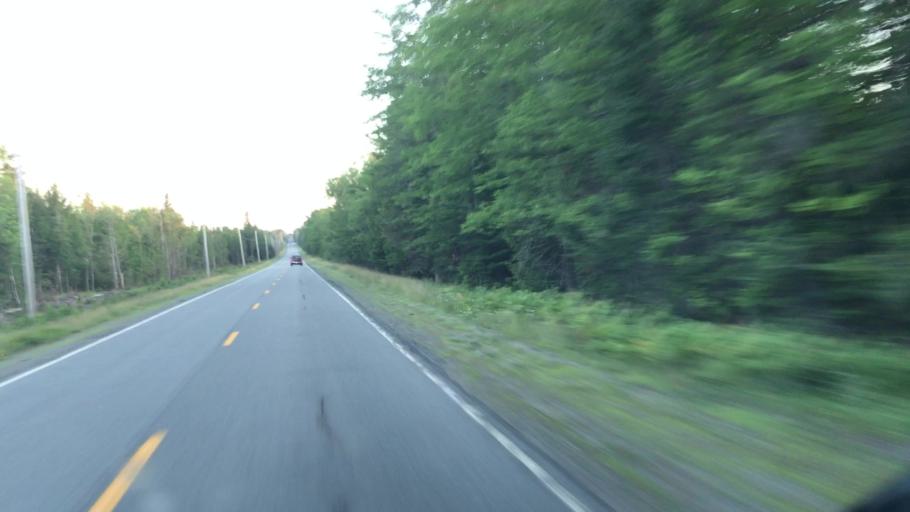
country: US
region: Maine
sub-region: Penobscot County
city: Medway
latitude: 45.6087
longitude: -68.3064
